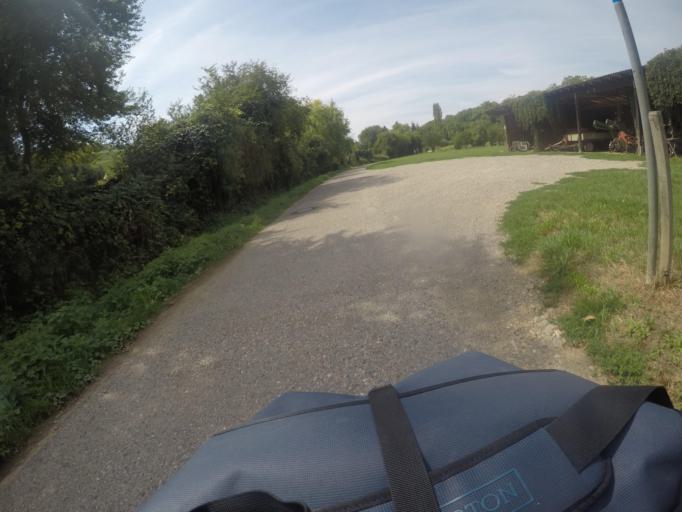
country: DE
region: Baden-Wuerttemberg
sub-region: Freiburg Region
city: Ebringen
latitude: 47.9751
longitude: 7.7910
